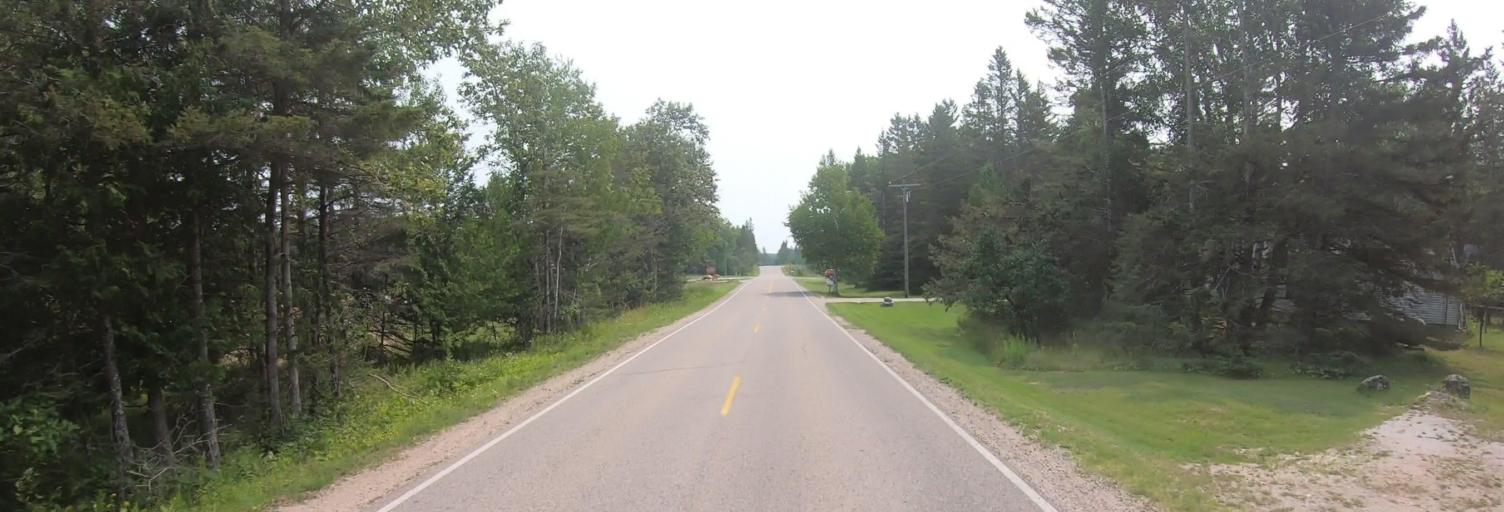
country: CA
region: Ontario
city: Thessalon
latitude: 45.9749
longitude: -83.6599
